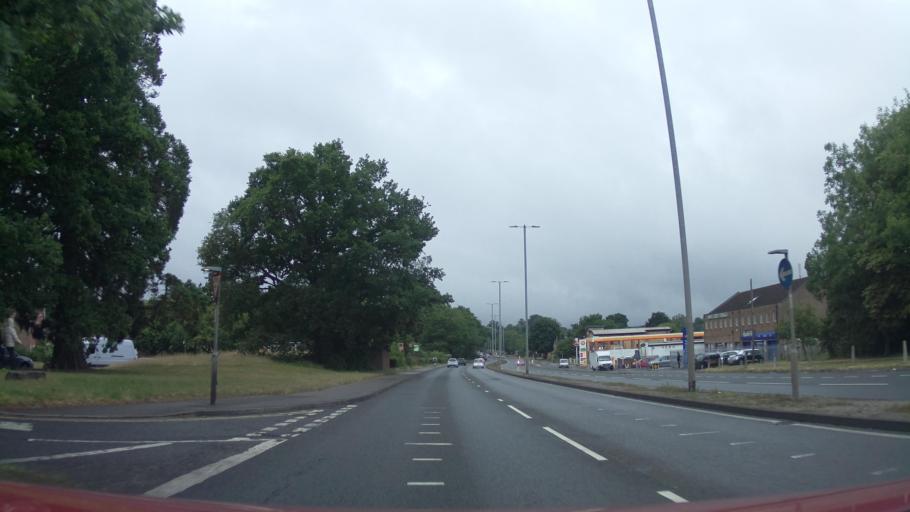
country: GB
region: England
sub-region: Bracknell Forest
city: Bracknell
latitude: 51.4054
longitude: -0.7451
